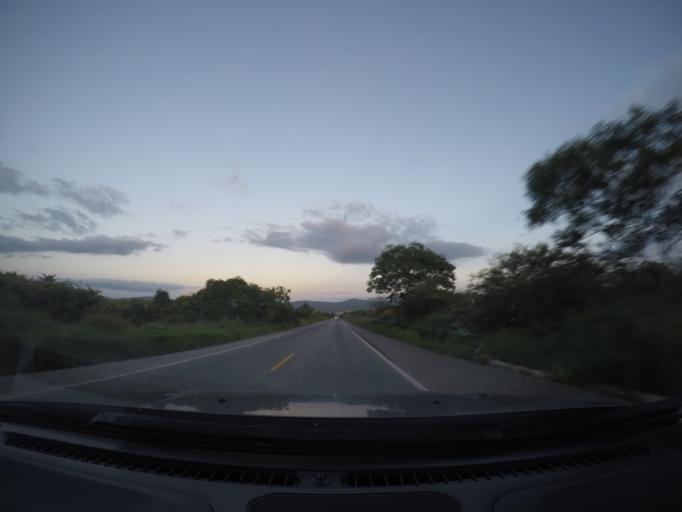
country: BR
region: Bahia
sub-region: Seabra
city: Seabra
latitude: -12.4310
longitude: -41.7974
